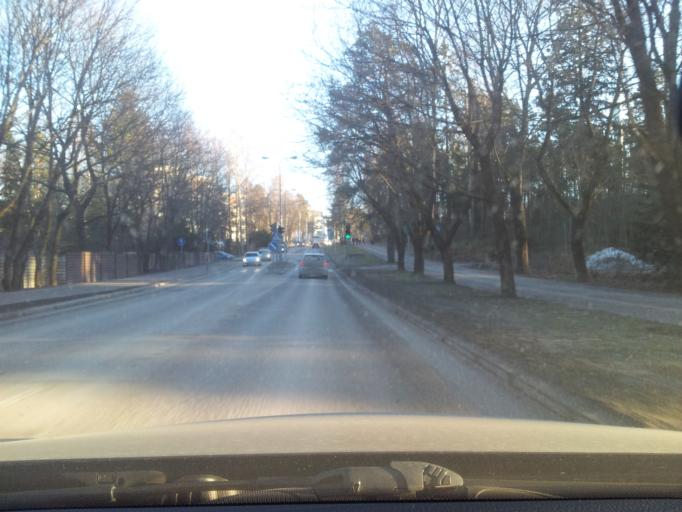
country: FI
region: Uusimaa
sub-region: Helsinki
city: Otaniemi
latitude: 60.1811
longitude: 24.7965
